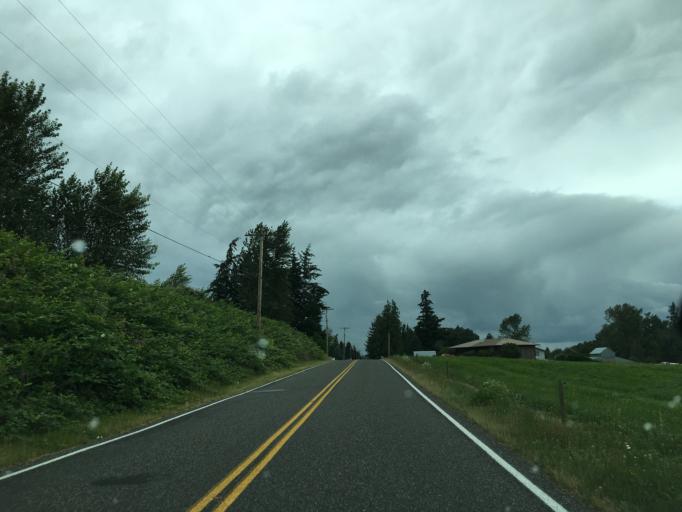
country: US
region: Washington
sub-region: Whatcom County
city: Nooksack
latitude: 48.9820
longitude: -122.3401
